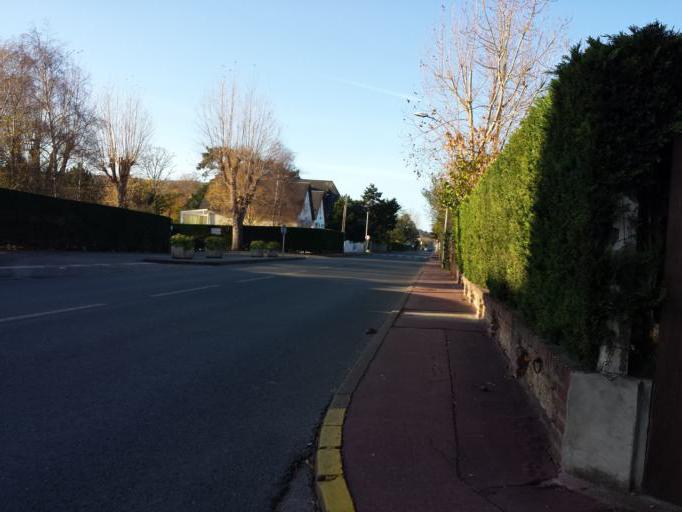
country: FR
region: Lower Normandy
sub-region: Departement du Calvados
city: Deauville
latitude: 49.3512
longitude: 0.0571
